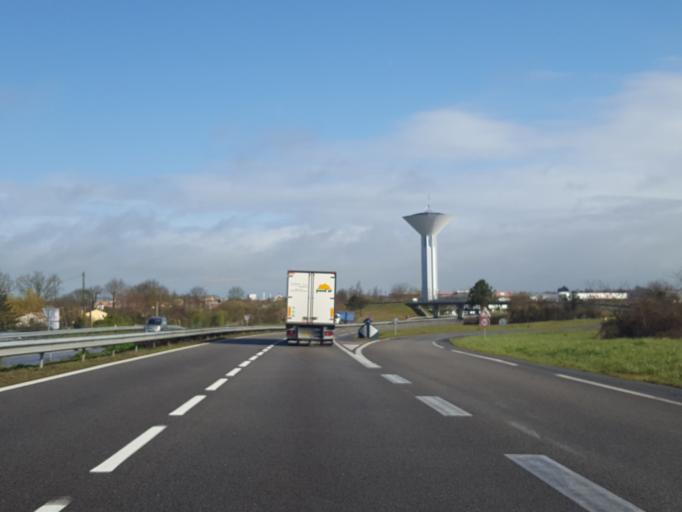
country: FR
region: Pays de la Loire
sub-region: Departement de la Vendee
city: Belleville-sur-Vie
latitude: 46.7676
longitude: -1.4308
